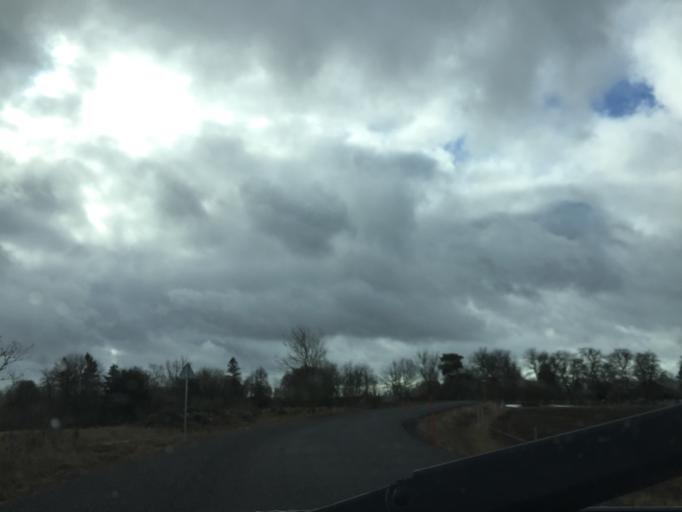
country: EE
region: Laeaene
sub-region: Haapsalu linn
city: Haapsalu
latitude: 58.6769
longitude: 23.5438
